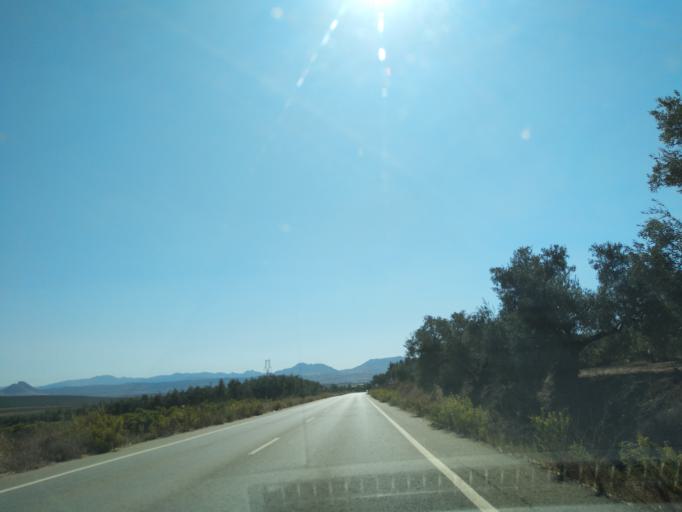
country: ES
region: Andalusia
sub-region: Provincia de Malaga
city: Mollina
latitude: 37.1063
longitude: -4.6388
